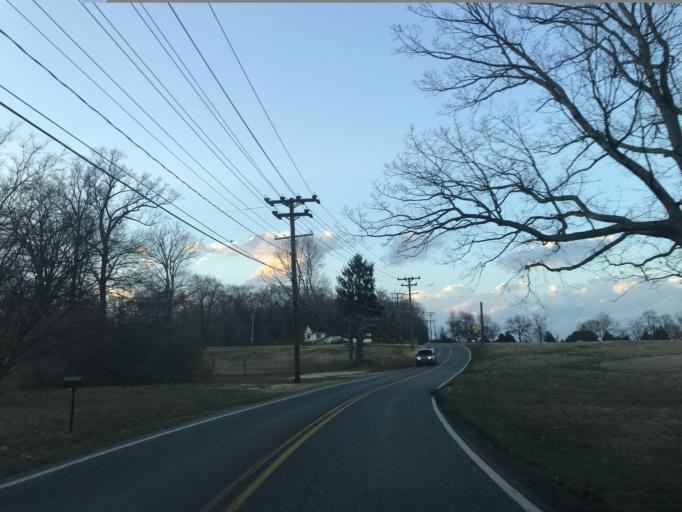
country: US
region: Maryland
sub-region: Harford County
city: Bel Air South
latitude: 39.5284
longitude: -76.2791
